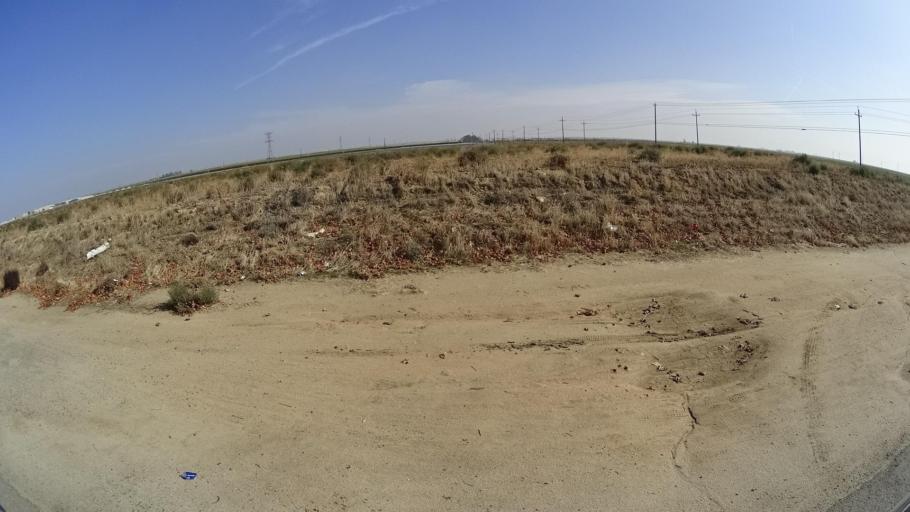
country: US
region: California
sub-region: Kern County
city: Greenacres
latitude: 35.5001
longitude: -119.1169
